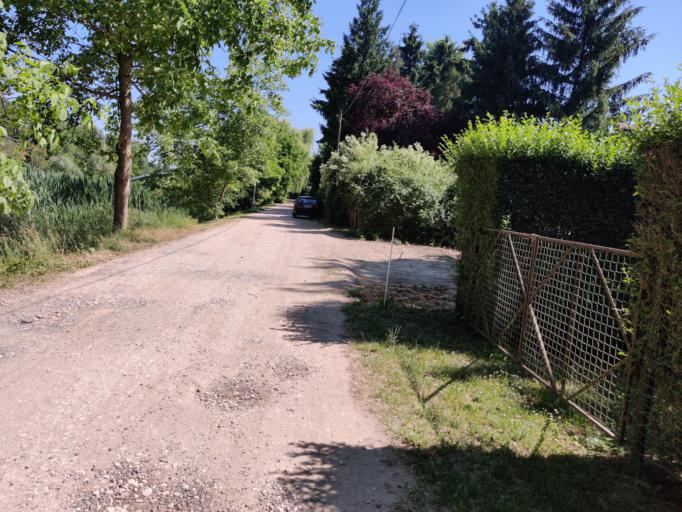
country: HU
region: Hajdu-Bihar
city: Balmazujvaros
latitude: 47.6014
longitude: 21.3778
